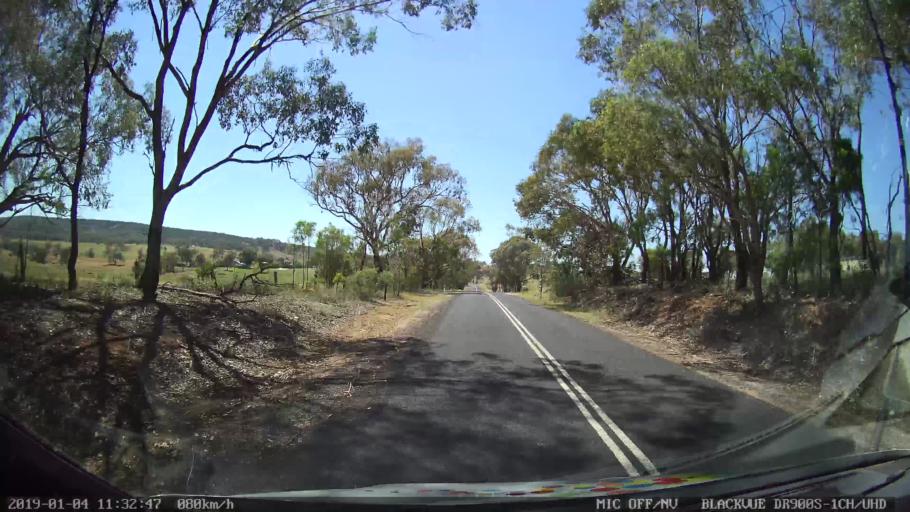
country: AU
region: New South Wales
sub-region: Cabonne
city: Molong
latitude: -33.0633
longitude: 148.8078
